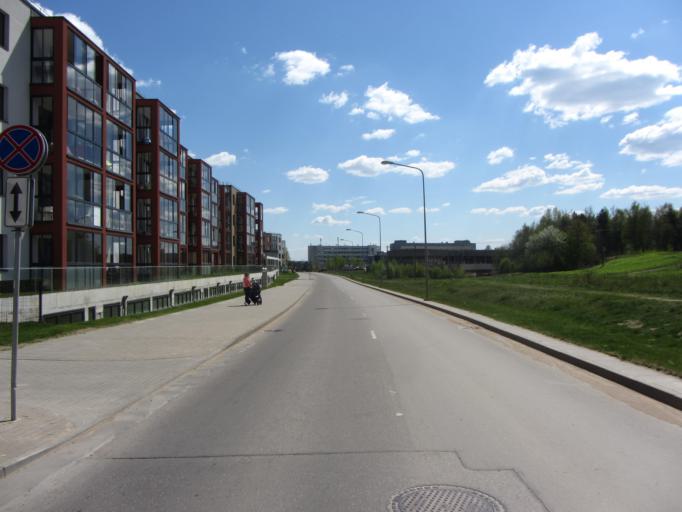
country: LT
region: Vilnius County
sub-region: Vilnius
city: Fabijoniskes
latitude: 54.7570
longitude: 25.2584
